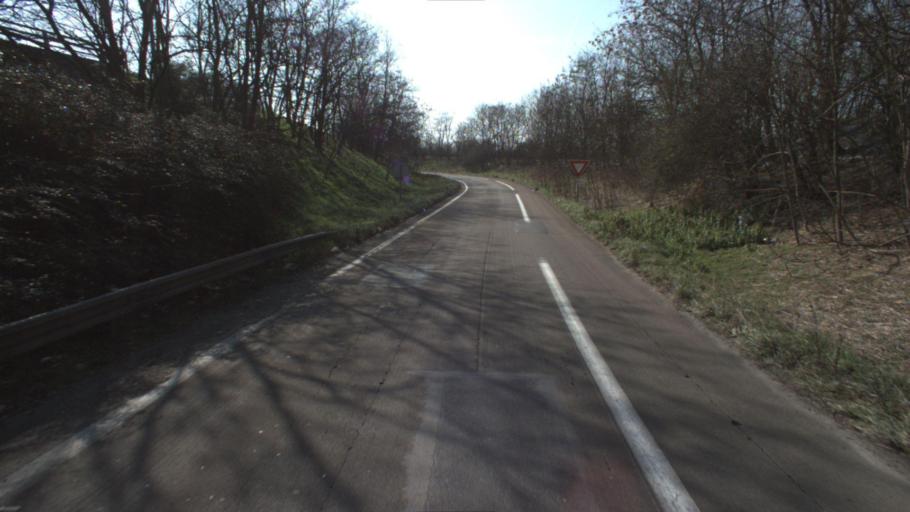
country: FR
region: Ile-de-France
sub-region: Departement de l'Essonne
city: Lisses
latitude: 48.6106
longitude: 2.4312
